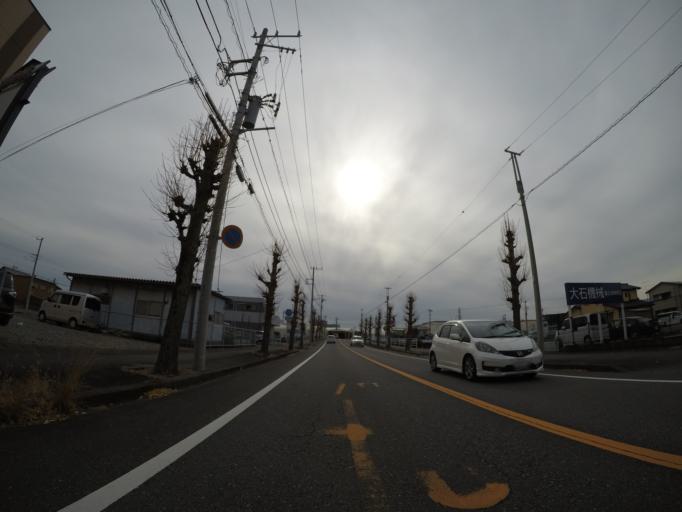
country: JP
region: Shizuoka
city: Fuji
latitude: 35.1528
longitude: 138.6828
